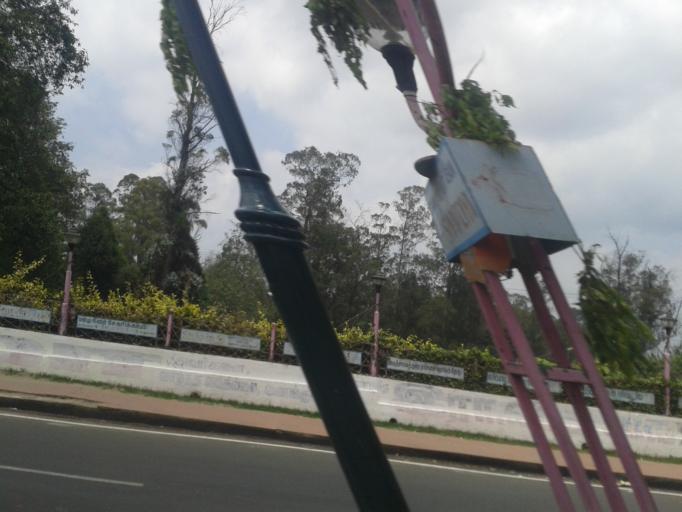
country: IN
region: Tamil Nadu
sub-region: Dindigul
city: Kodaikanal
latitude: 10.2376
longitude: 77.4887
